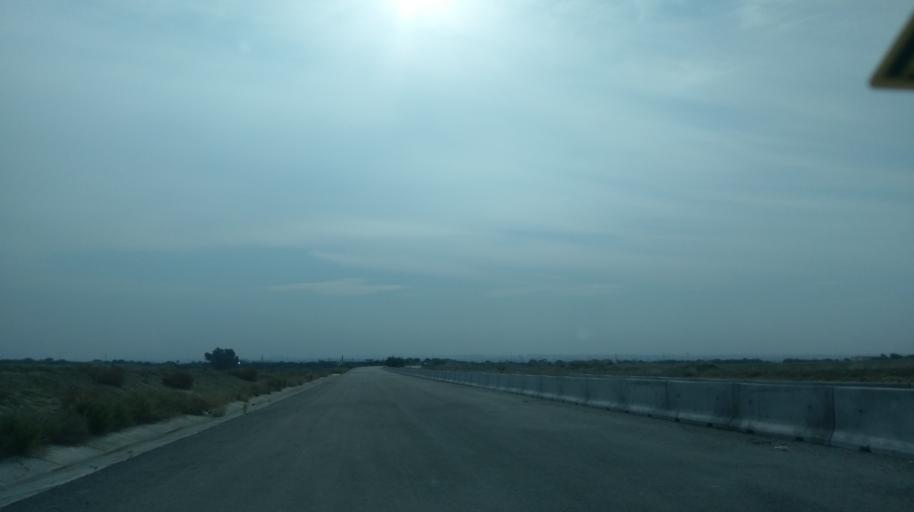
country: CY
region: Lefkosia
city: Nicosia
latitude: 35.2208
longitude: 33.4015
